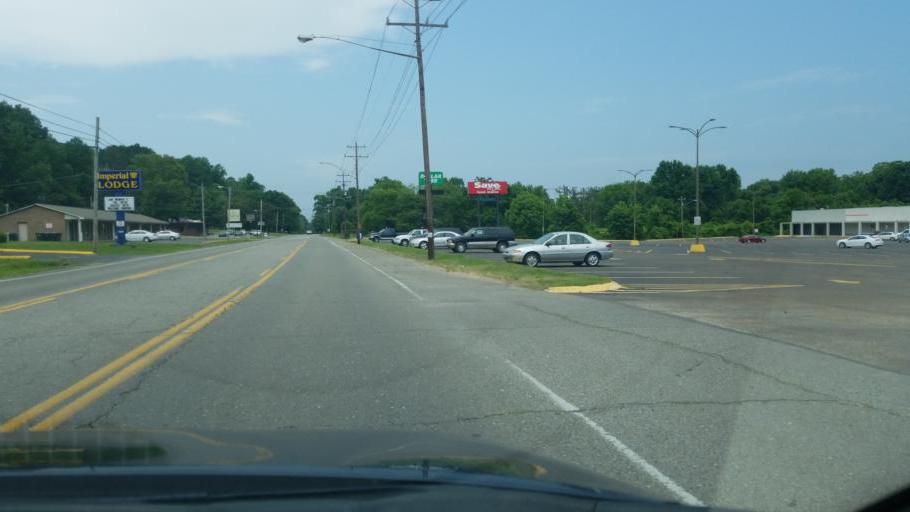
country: US
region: Tennessee
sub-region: Humphreys County
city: Waverly
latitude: 36.0834
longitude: -87.8097
